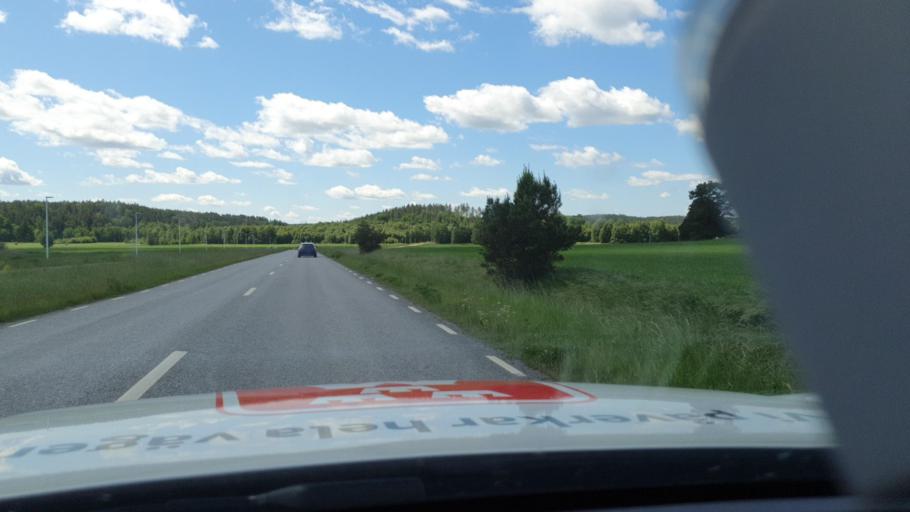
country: SE
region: Uppsala
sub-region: Knivsta Kommun
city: Knivsta
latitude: 59.7186
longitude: 17.7734
